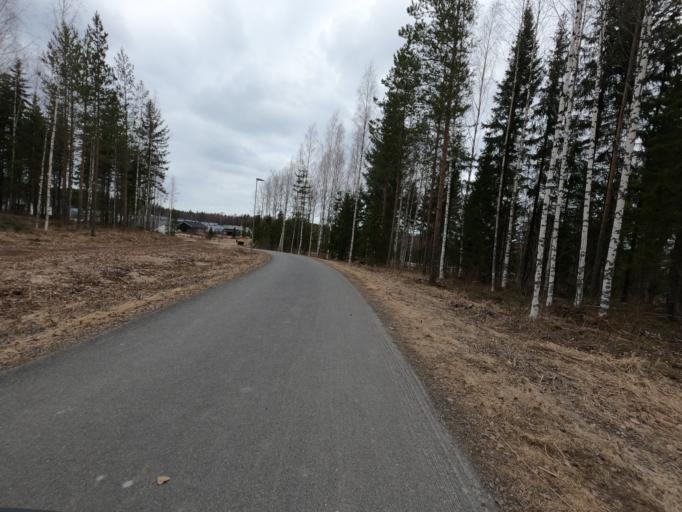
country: FI
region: North Karelia
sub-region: Joensuu
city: Joensuu
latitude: 62.5656
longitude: 29.8198
